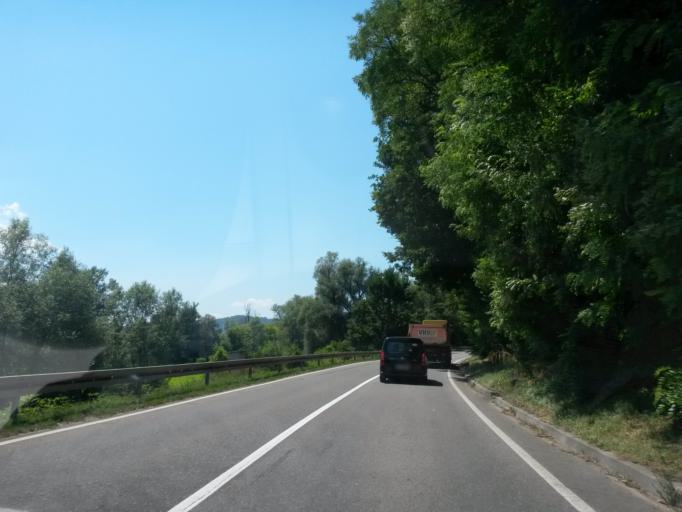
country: BA
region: Federation of Bosnia and Herzegovina
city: Odzak
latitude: 44.9377
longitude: 18.2039
